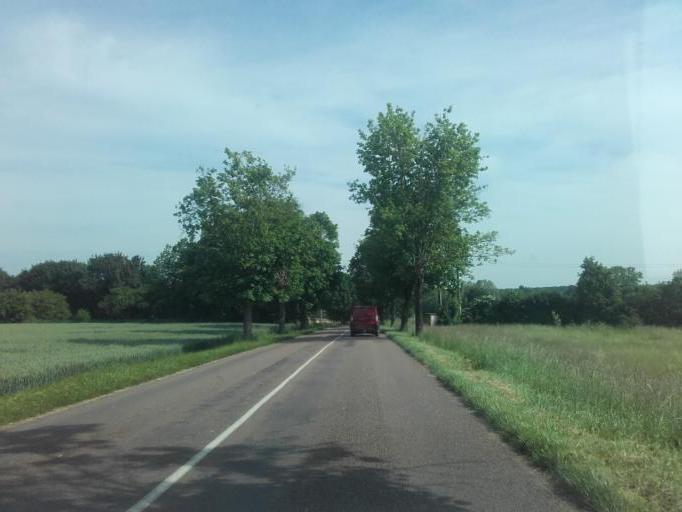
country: FR
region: Bourgogne
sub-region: Departement de Saone-et-Loire
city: Dracy-le-Fort
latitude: 46.8017
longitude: 4.7523
